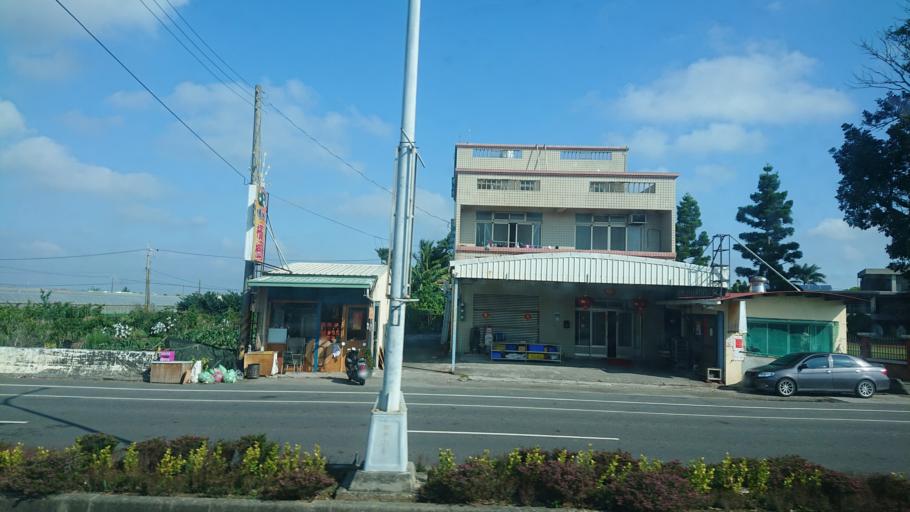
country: TW
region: Taiwan
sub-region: Chiayi
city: Taibao
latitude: 23.4580
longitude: 120.3070
